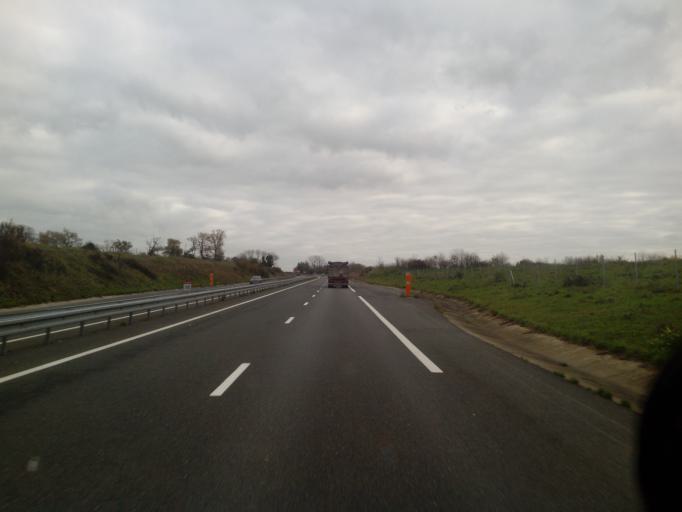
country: FR
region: Poitou-Charentes
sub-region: Departement des Deux-Sevres
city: Saint-Pierre-des-Echaubrognes
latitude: 46.9543
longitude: -0.7758
